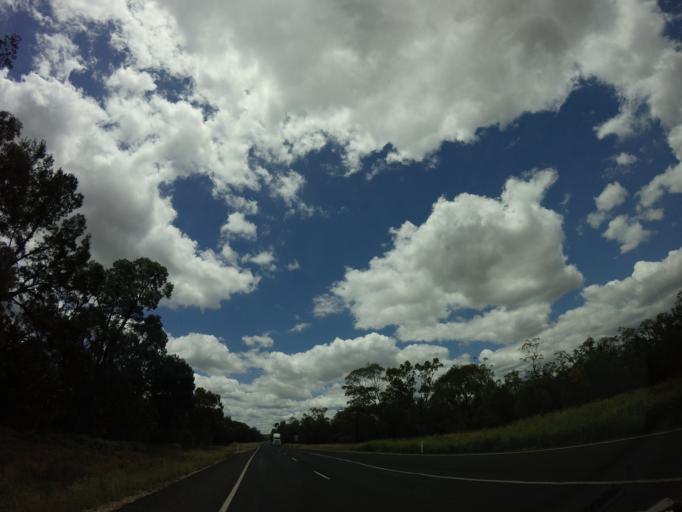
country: AU
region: Queensland
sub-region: Goondiwindi
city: Goondiwindi
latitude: -28.0457
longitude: 150.7895
